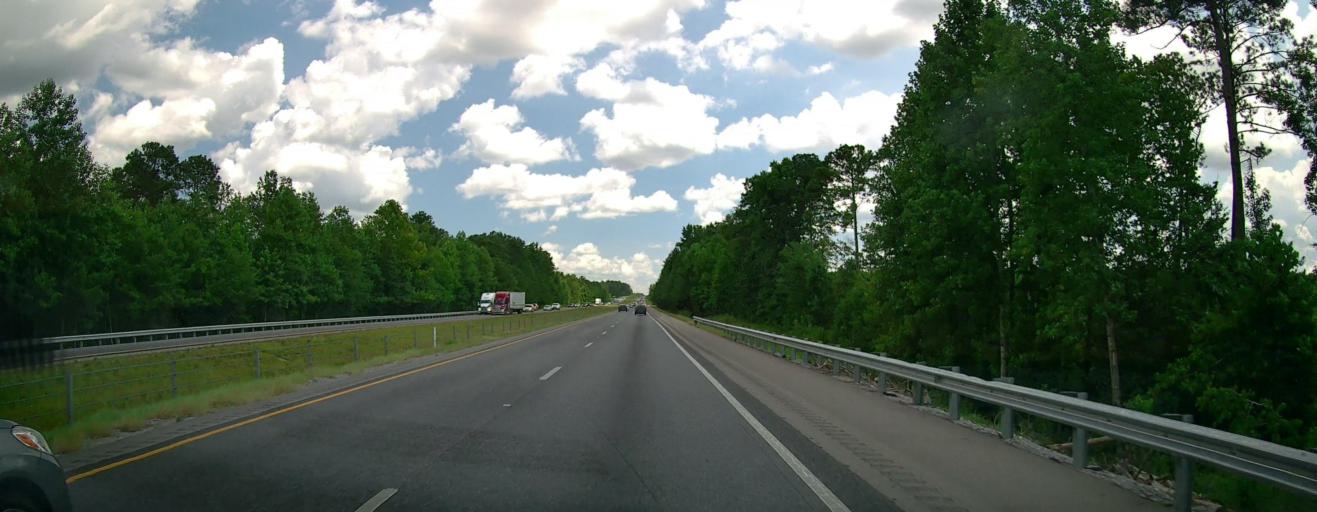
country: US
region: Alabama
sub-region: Autauga County
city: Marbury
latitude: 32.7141
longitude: -86.5289
